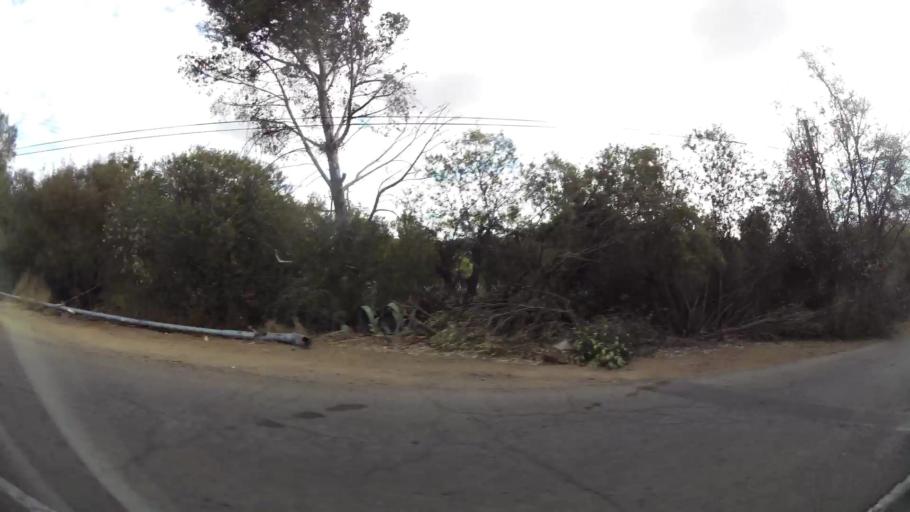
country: ZA
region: Orange Free State
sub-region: Mangaung Metropolitan Municipality
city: Bloemfontein
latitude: -29.0737
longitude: 26.2064
